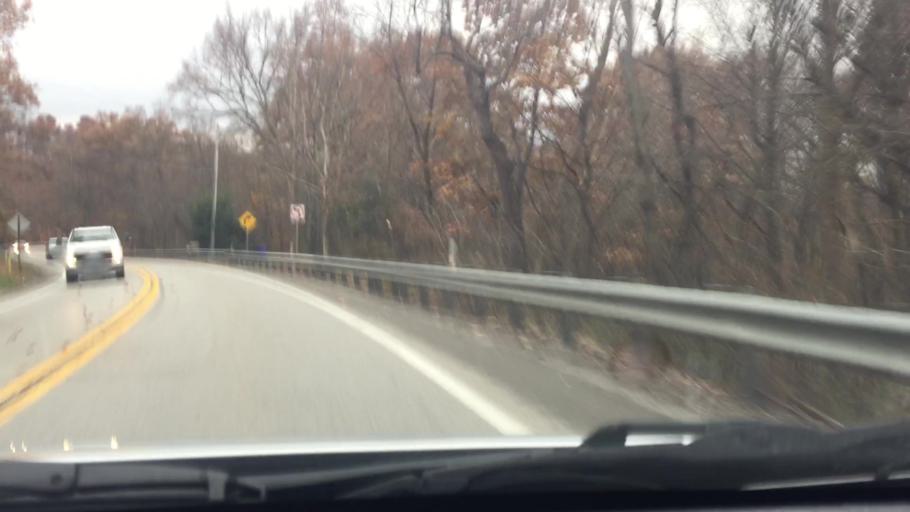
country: US
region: Pennsylvania
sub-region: Butler County
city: Saxonburg
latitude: 40.7233
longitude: -79.8793
